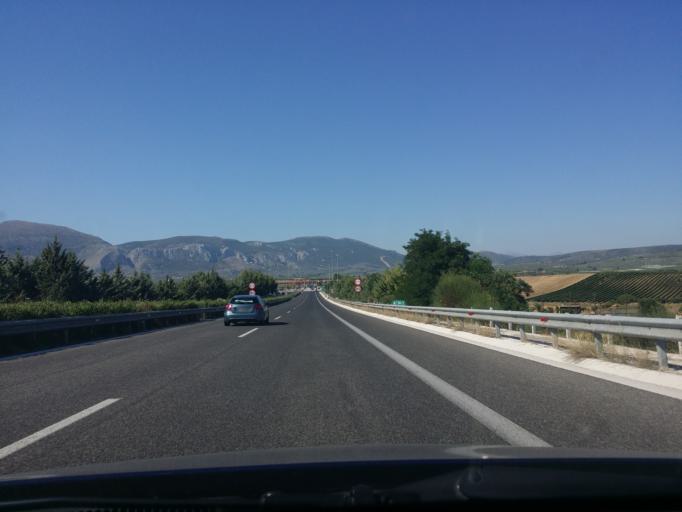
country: GR
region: Peloponnese
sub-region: Nomos Korinthias
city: Ayios Vasilios
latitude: 37.8409
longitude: 22.8115
